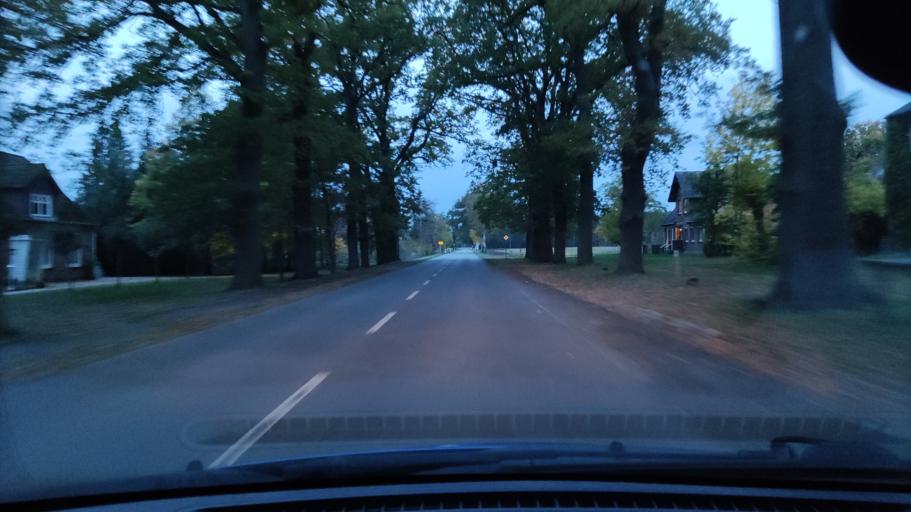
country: DE
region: Lower Saxony
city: Trebel
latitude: 52.9589
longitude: 11.3264
